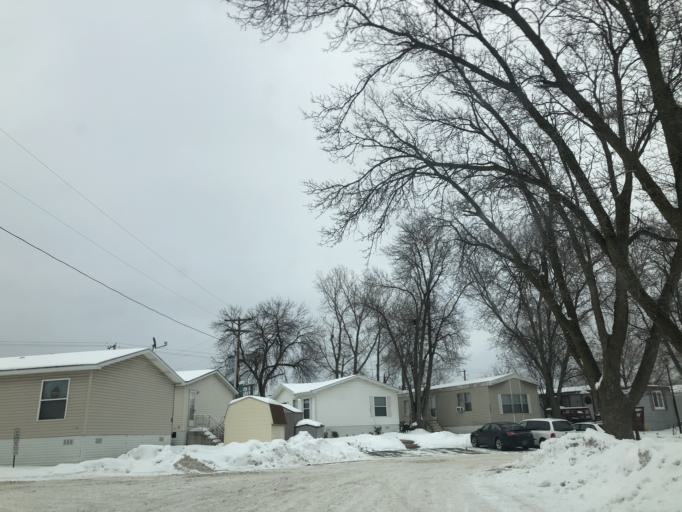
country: US
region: Minnesota
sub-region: Ramsey County
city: New Brighton
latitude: 45.0844
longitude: -93.1842
